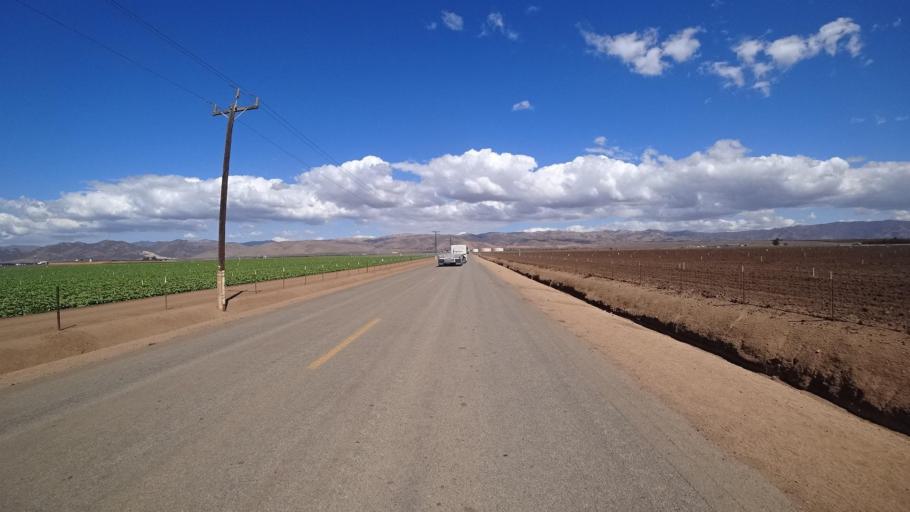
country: US
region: California
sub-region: Monterey County
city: Gonzales
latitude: 36.5172
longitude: -121.4265
